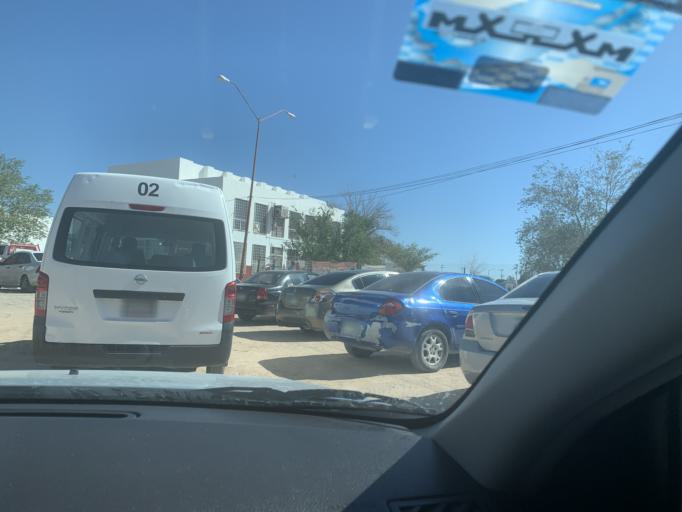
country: US
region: Texas
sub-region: El Paso County
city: Socorro Mission Number 1 Colonia
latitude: 31.5926
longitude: -106.3685
